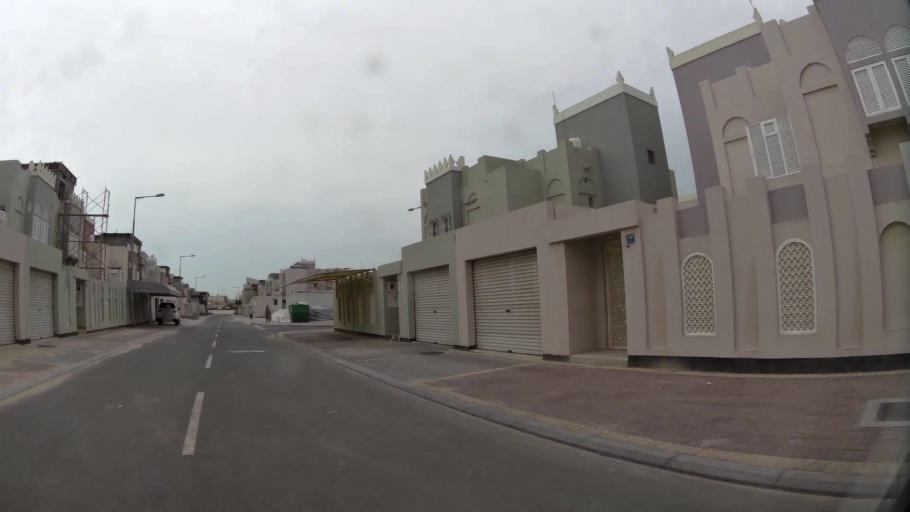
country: BH
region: Northern
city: Madinat `Isa
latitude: 26.1666
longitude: 50.5397
